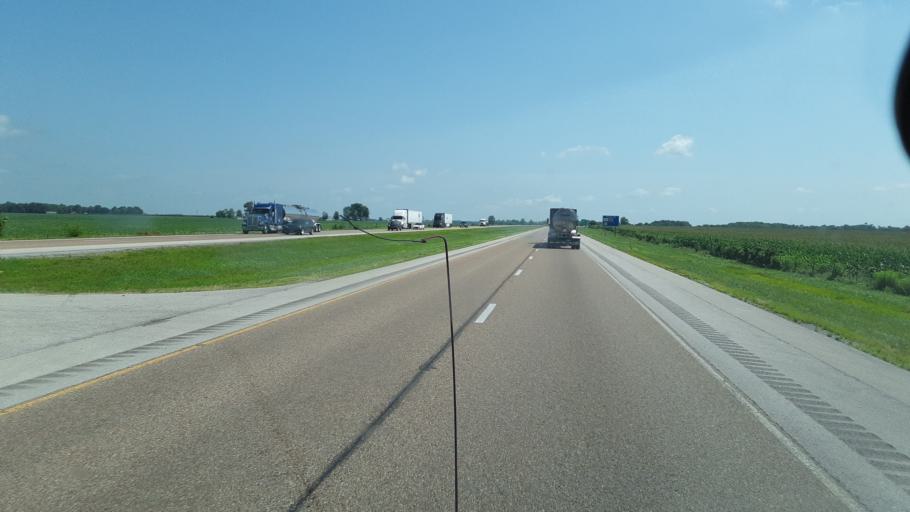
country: US
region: Illinois
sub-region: Clark County
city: Casey
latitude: 39.3101
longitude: -88.0107
